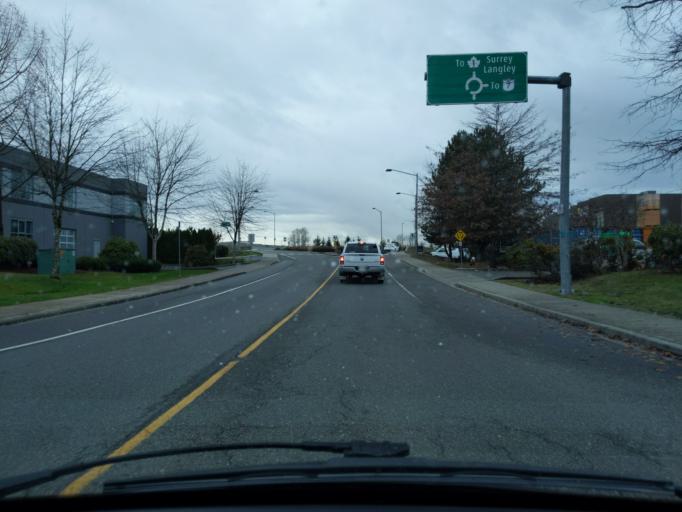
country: CA
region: British Columbia
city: Pitt Meadows
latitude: 49.2094
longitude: -122.6658
